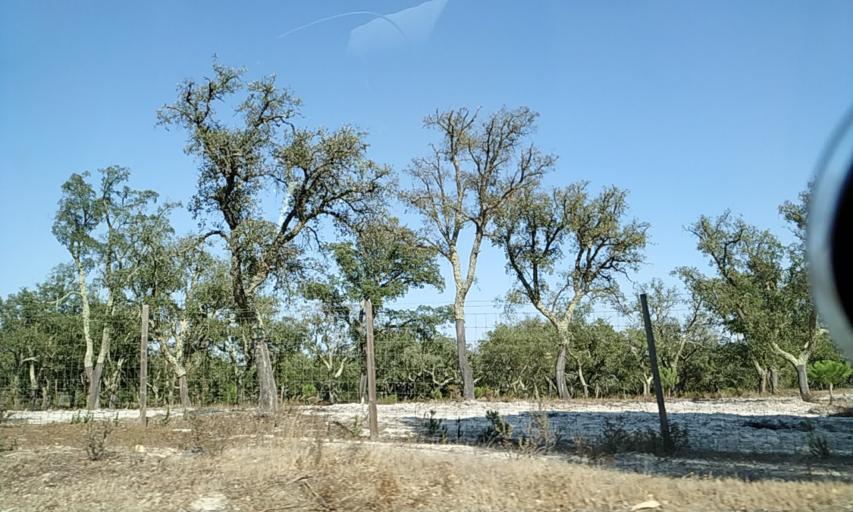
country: PT
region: Santarem
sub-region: Coruche
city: Coruche
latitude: 38.8135
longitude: -8.5749
